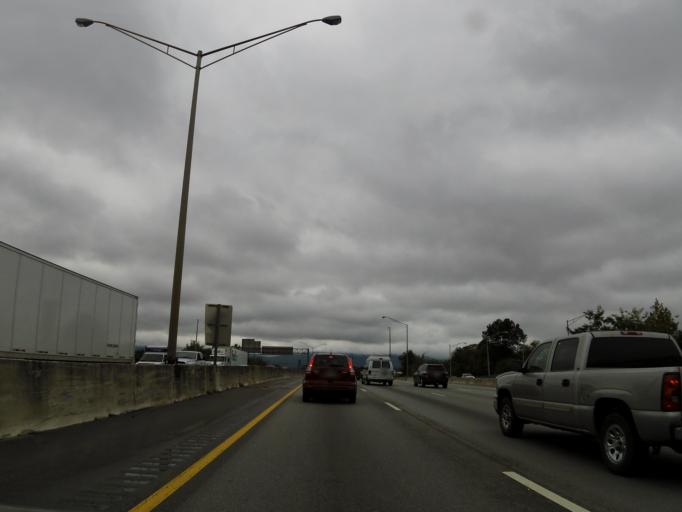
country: US
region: Tennessee
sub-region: Hamilton County
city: Chattanooga
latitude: 35.0252
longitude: -85.3019
